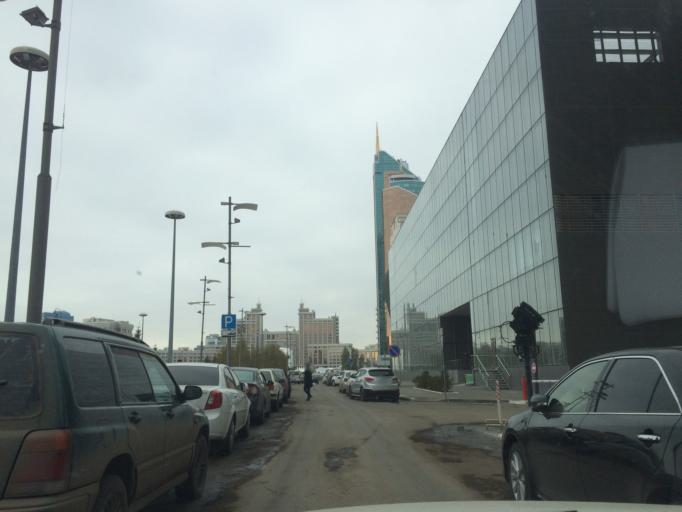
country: KZ
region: Astana Qalasy
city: Astana
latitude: 51.1302
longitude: 71.4210
